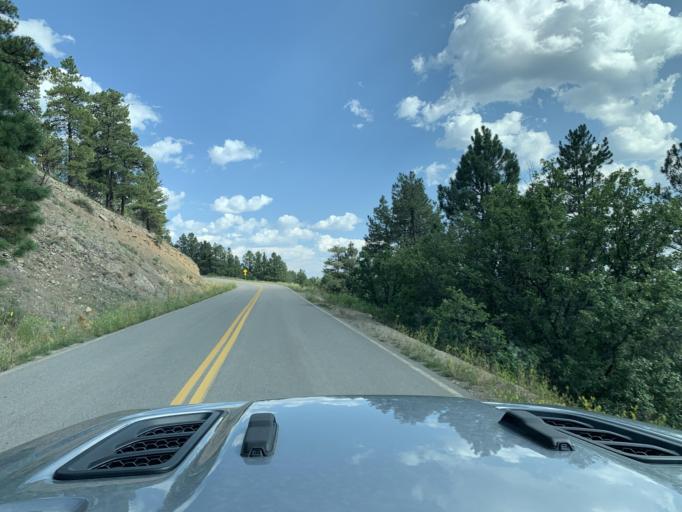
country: US
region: Colorado
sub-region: Archuleta County
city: Pagosa Springs
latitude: 37.2415
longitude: -107.0275
